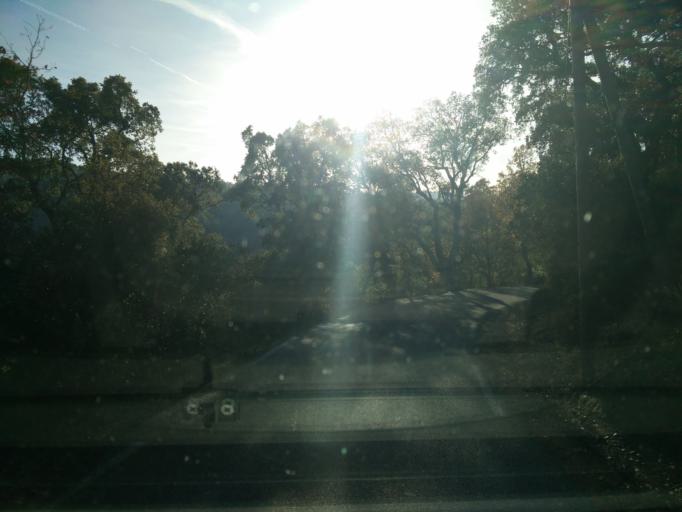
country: FR
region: Provence-Alpes-Cote d'Azur
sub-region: Departement du Var
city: La Garde-Freinet
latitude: 43.3405
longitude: 6.4829
